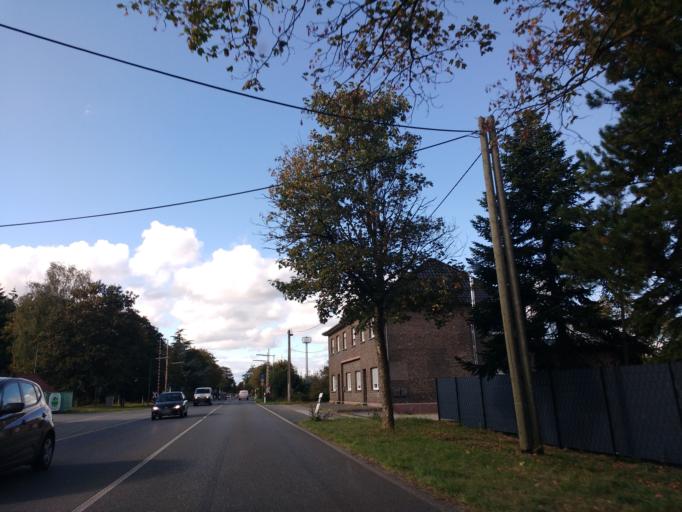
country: DE
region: North Rhine-Westphalia
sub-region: Regierungsbezirk Dusseldorf
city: Alpen
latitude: 51.6050
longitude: 6.5207
